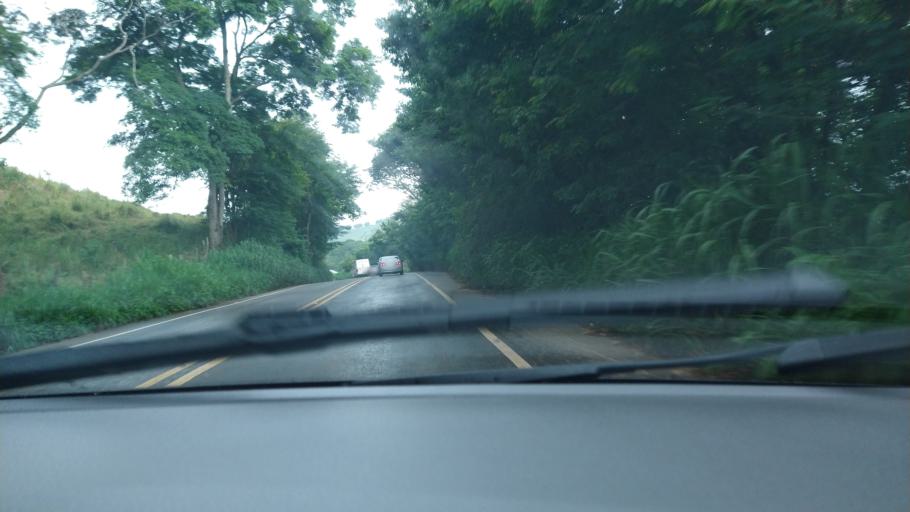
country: BR
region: Minas Gerais
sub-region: Vicosa
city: Vicosa
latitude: -20.6534
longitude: -42.8603
